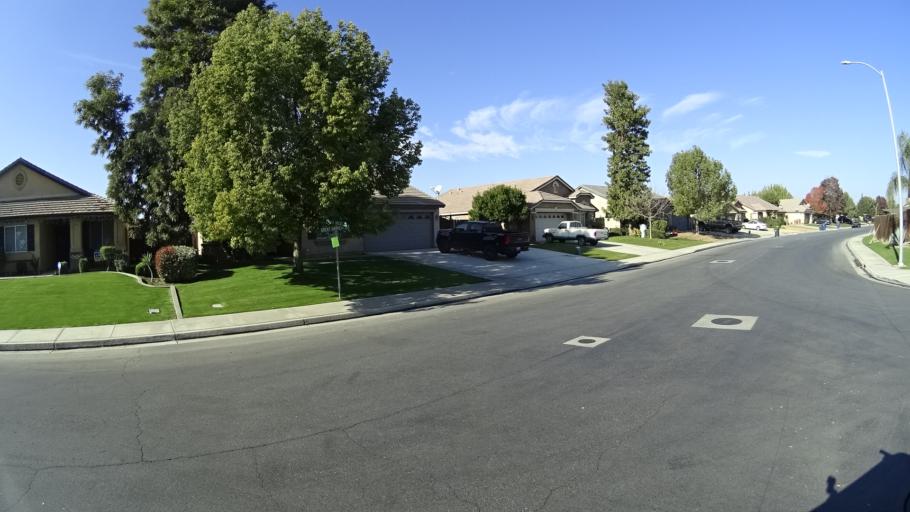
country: US
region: California
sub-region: Kern County
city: Greenfield
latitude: 35.2719
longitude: -119.0615
